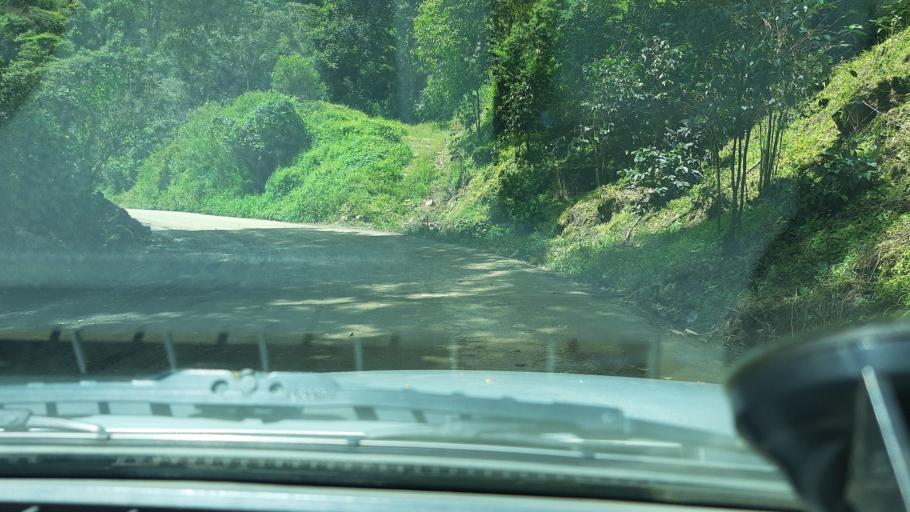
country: CO
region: Boyaca
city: Chinavita
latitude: 5.1838
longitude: -73.3824
